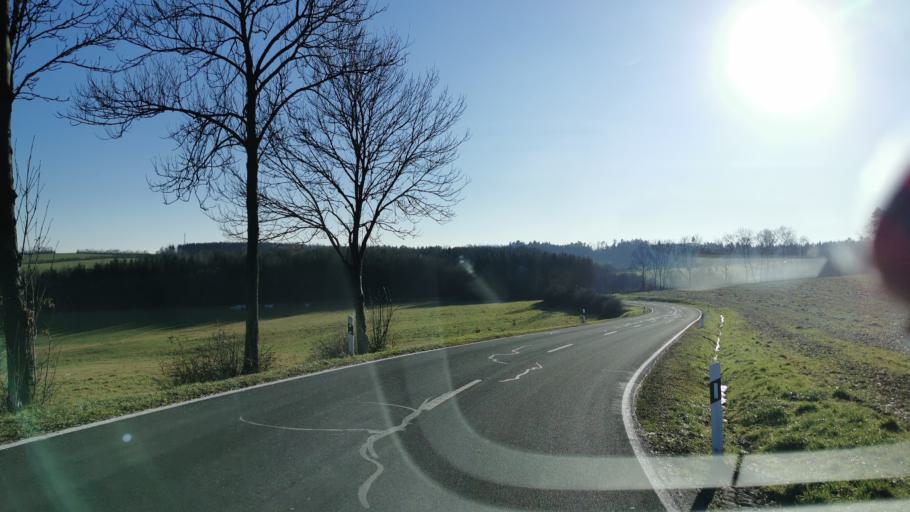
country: DE
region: Rheinland-Pfalz
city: Utzerath
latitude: 50.2166
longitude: 6.9326
